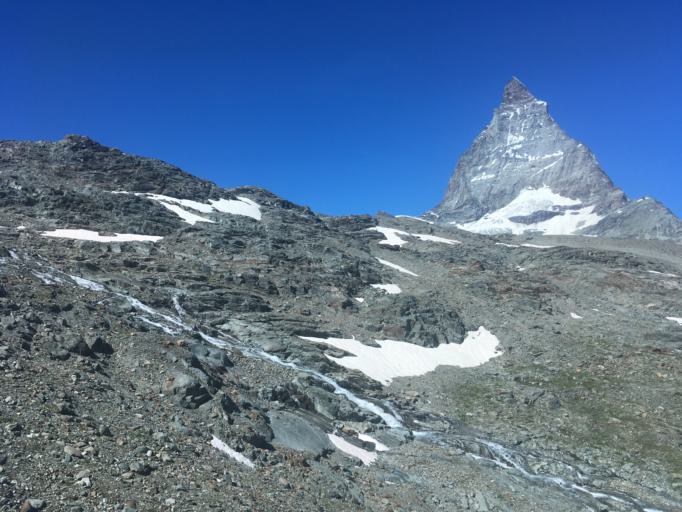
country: CH
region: Valais
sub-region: Visp District
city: Zermatt
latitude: 45.9779
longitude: 7.7172
